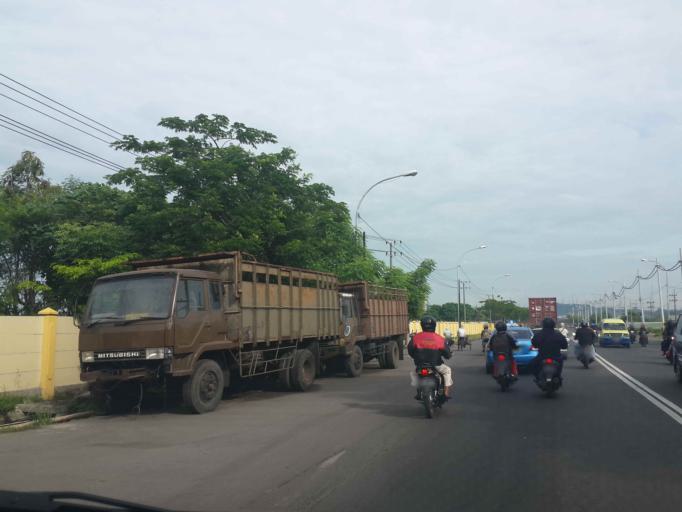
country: ID
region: East Java
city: Kebomas
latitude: -7.2095
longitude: 112.6519
